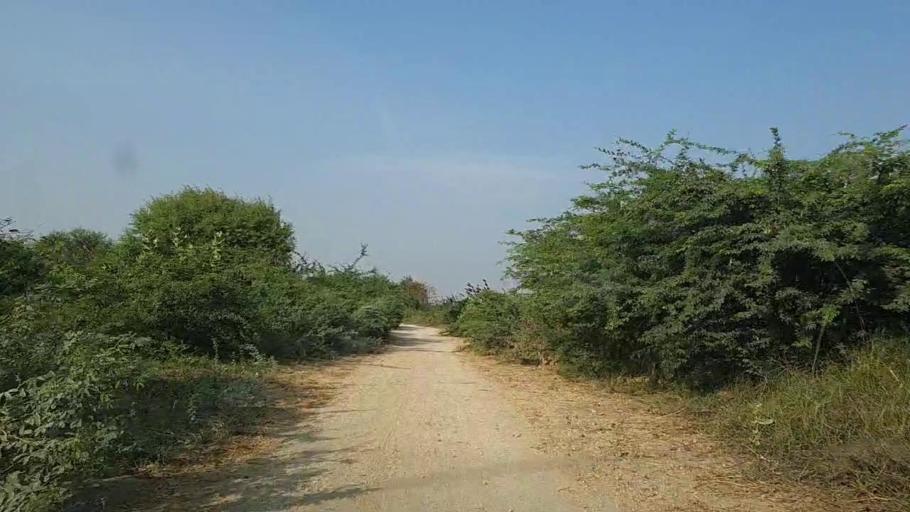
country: PK
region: Sindh
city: Mirpur Sakro
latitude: 24.5970
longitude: 67.6489
